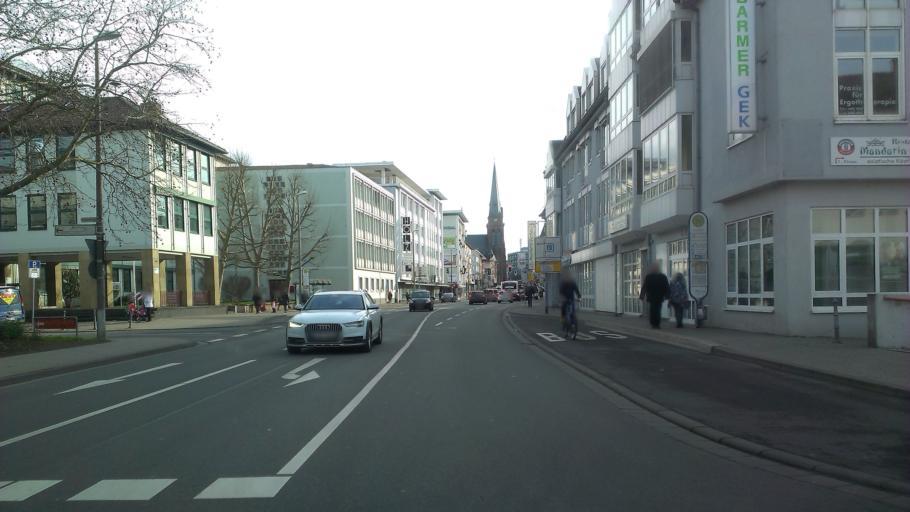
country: DE
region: Rheinland-Pfalz
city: Bad Kreuznach
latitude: 49.8457
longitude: 7.8604
